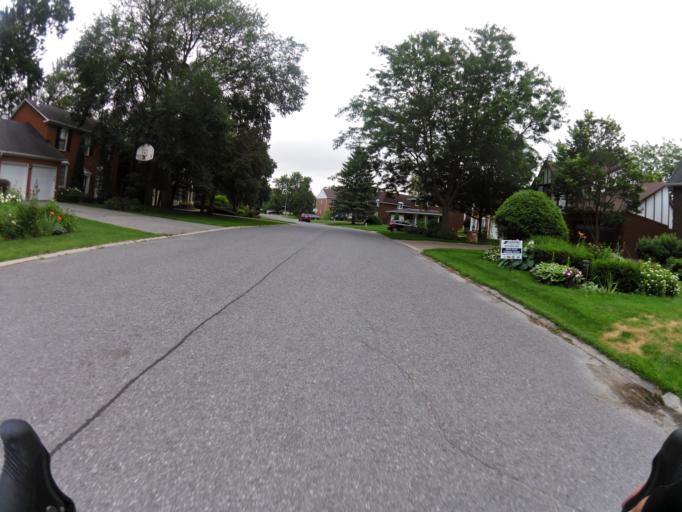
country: CA
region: Ontario
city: Ottawa
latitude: 45.3236
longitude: -75.7071
